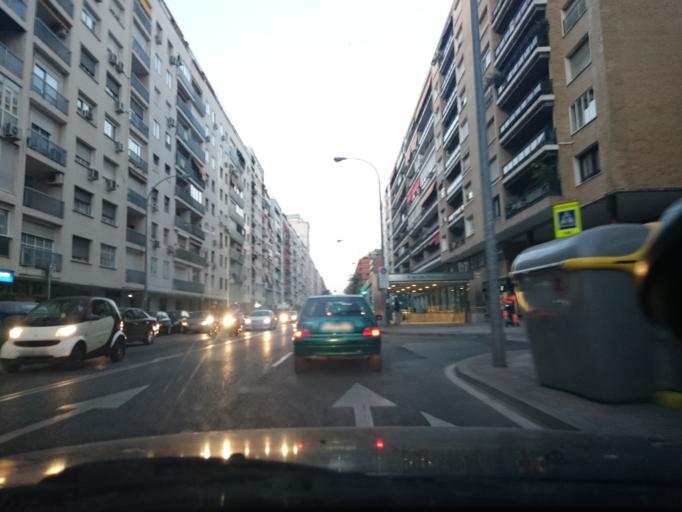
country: ES
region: Andalusia
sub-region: Provincia de Sevilla
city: Sevilla
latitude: 37.3764
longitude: -6.0050
